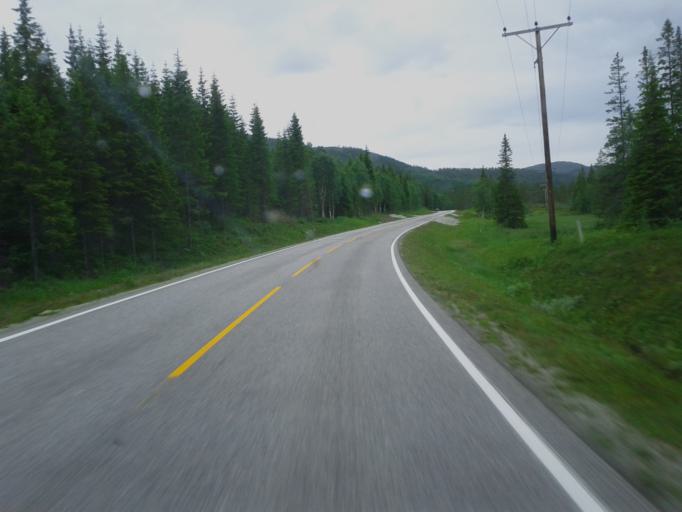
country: NO
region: Nord-Trondelag
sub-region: Namsskogan
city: Namsskogan
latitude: 64.8740
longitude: 13.0674
